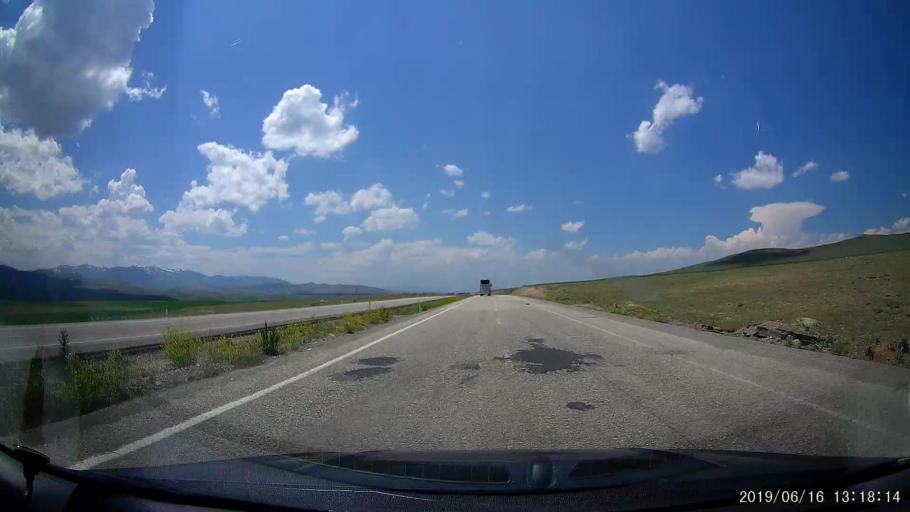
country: TR
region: Agri
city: Taslicay
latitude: 39.6297
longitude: 43.4352
